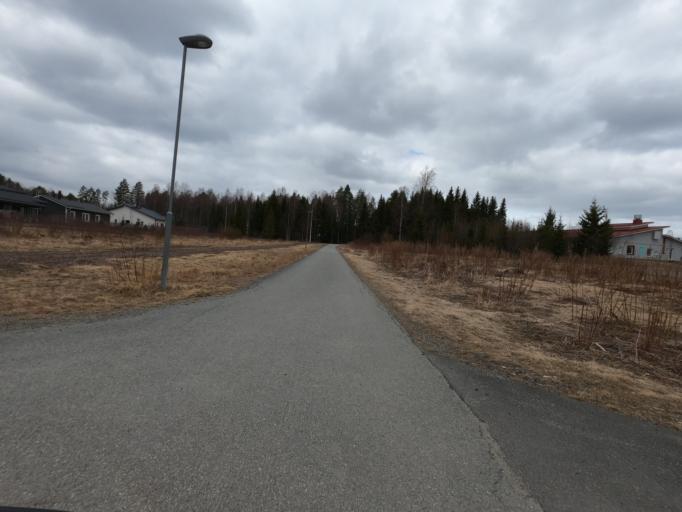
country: FI
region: North Karelia
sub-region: Joensuu
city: Joensuu
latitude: 62.5686
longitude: 29.8151
